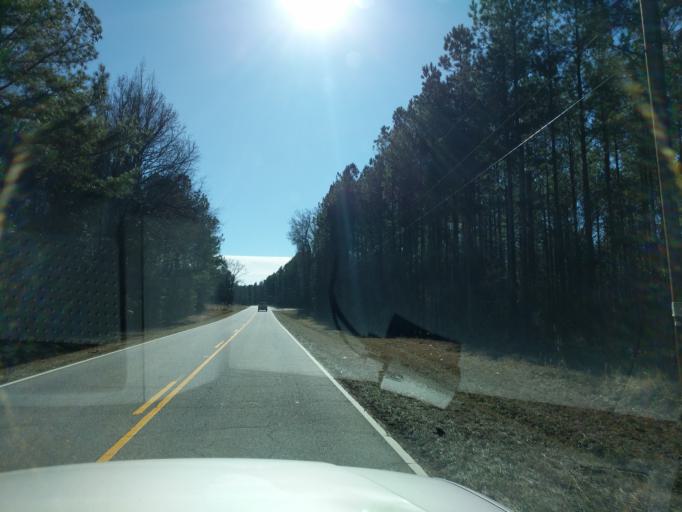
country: US
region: South Carolina
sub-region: Saluda County
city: Saluda
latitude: 34.1280
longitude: -81.8402
